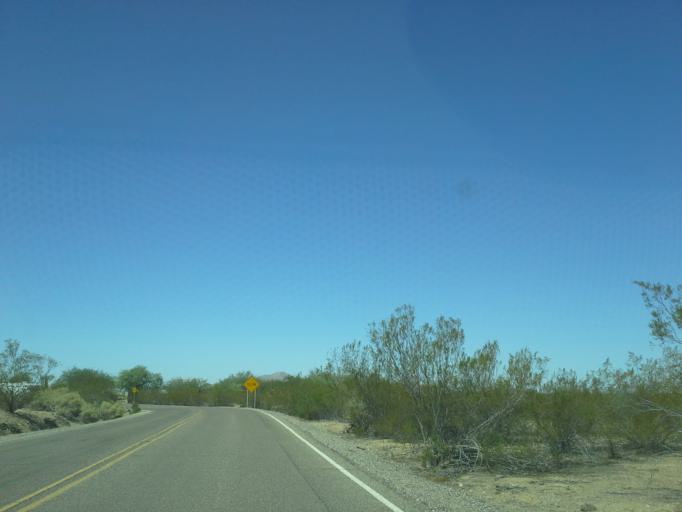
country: US
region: Arizona
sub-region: Pinal County
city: Coolidge
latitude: 32.9955
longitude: -111.5345
